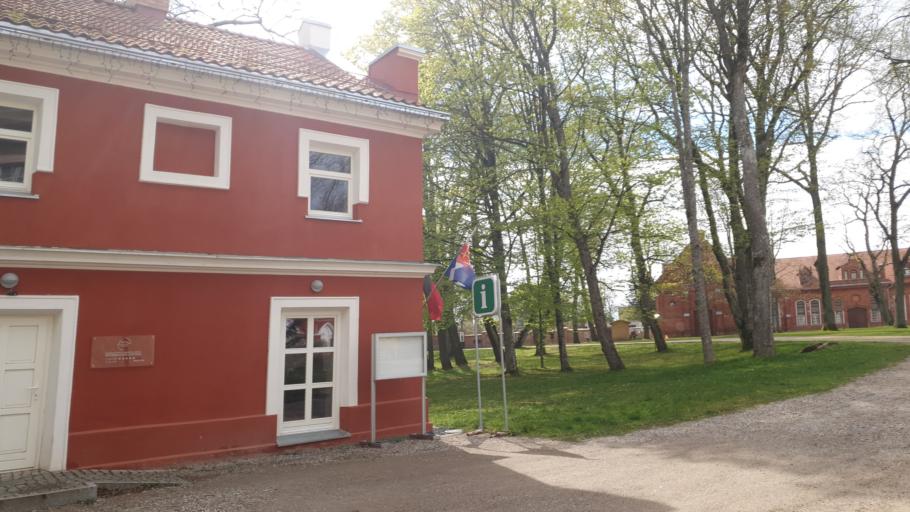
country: LT
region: Kauno apskritis
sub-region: Kauno rajonas
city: Akademija (Kaunas)
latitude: 54.9430
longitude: 23.7833
